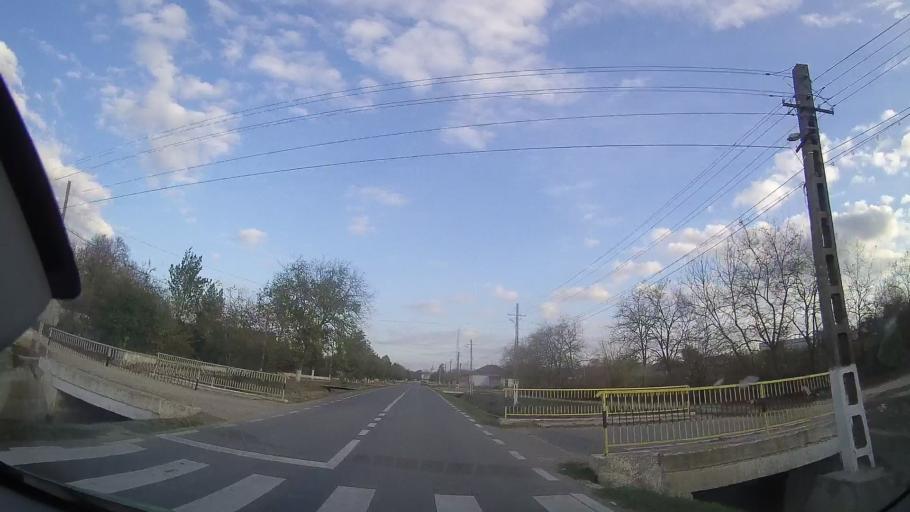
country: RO
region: Constanta
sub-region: Comuna Independenta
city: Independenta
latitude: 43.9533
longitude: 28.0786
